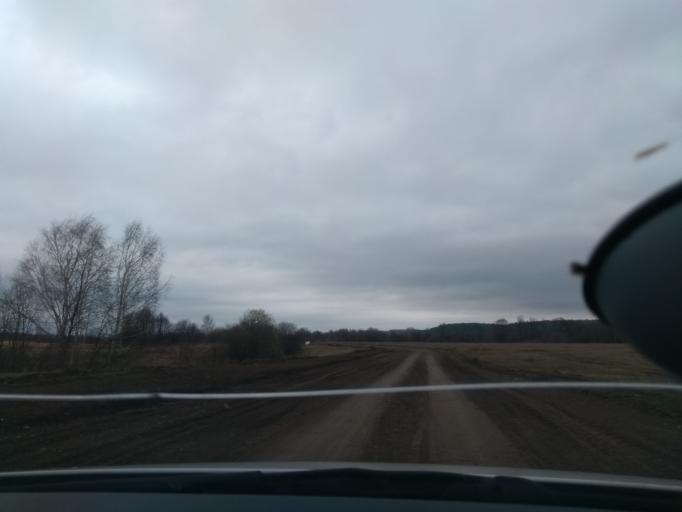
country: RU
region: Perm
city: Orda
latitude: 57.2330
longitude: 56.6091
